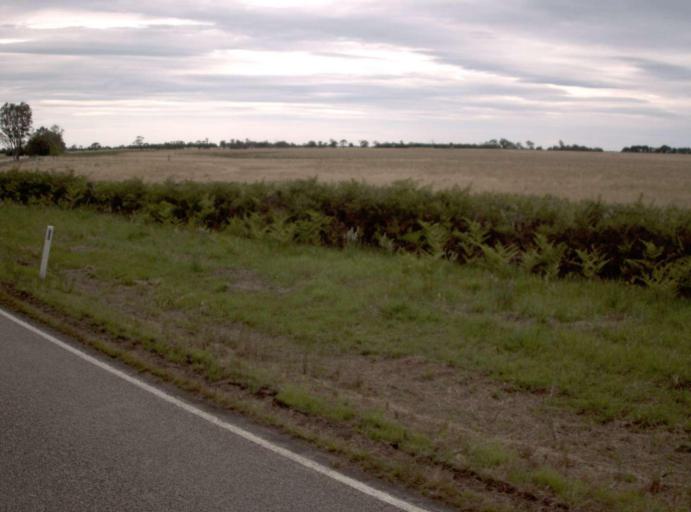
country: AU
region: Victoria
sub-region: East Gippsland
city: Bairnsdale
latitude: -37.9635
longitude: 147.4885
